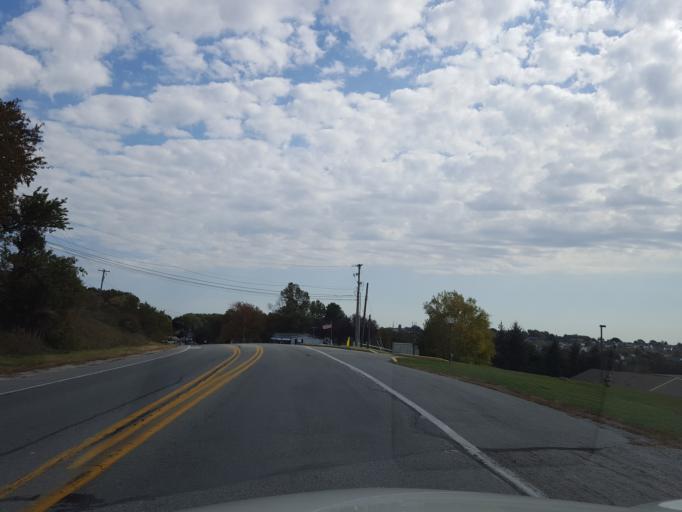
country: US
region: Pennsylvania
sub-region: York County
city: Yoe
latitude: 39.9102
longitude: -76.6225
